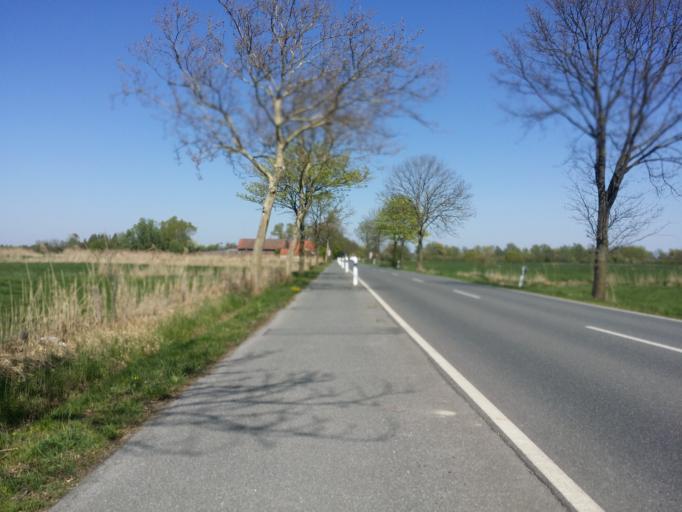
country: DE
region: Lower Saxony
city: Stuhr
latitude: 53.0384
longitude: 8.7634
